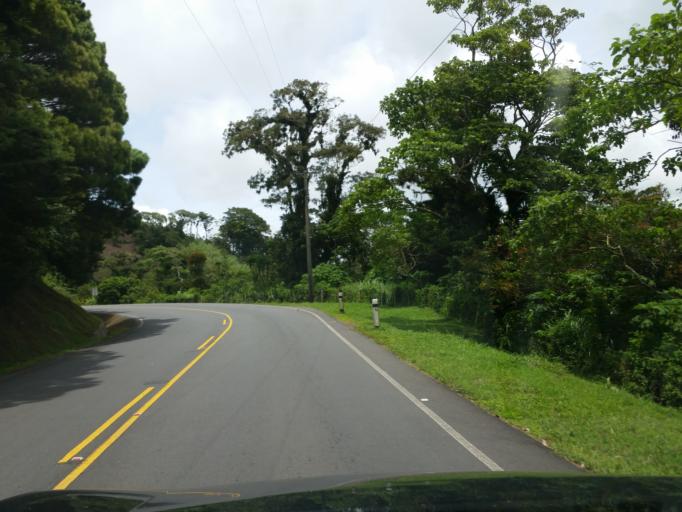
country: NI
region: Matagalpa
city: Matagalpa
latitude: 12.9936
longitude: -85.9208
